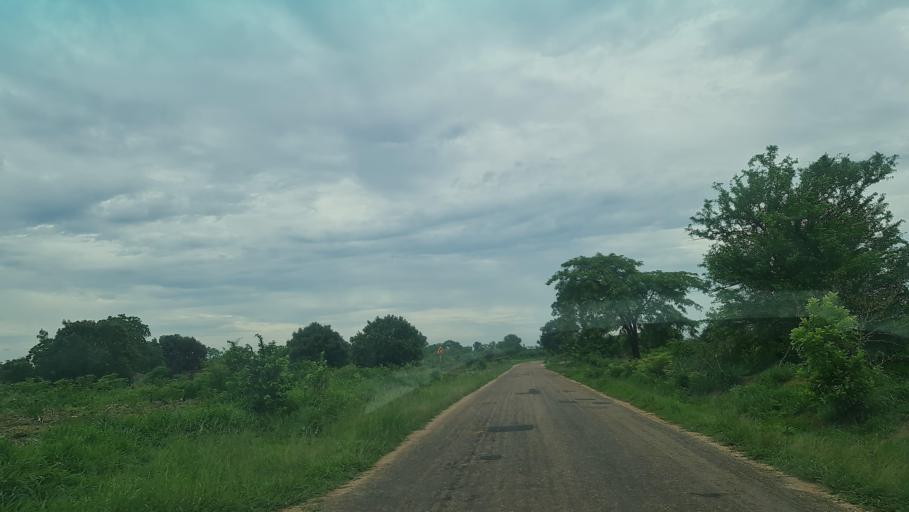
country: MW
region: Southern Region
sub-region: Nsanje District
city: Nsanje
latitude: -17.6927
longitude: 35.7366
